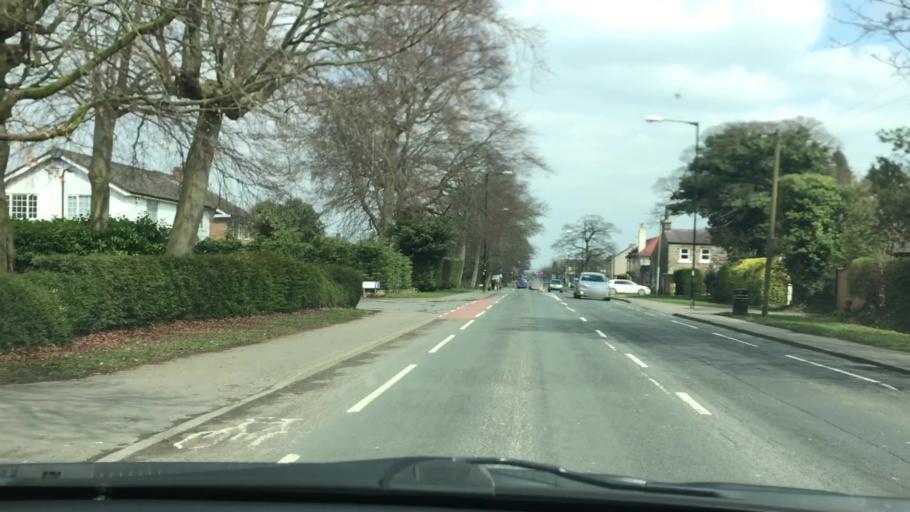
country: GB
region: England
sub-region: North Yorkshire
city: Harrogate
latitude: 53.9873
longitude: -1.5098
